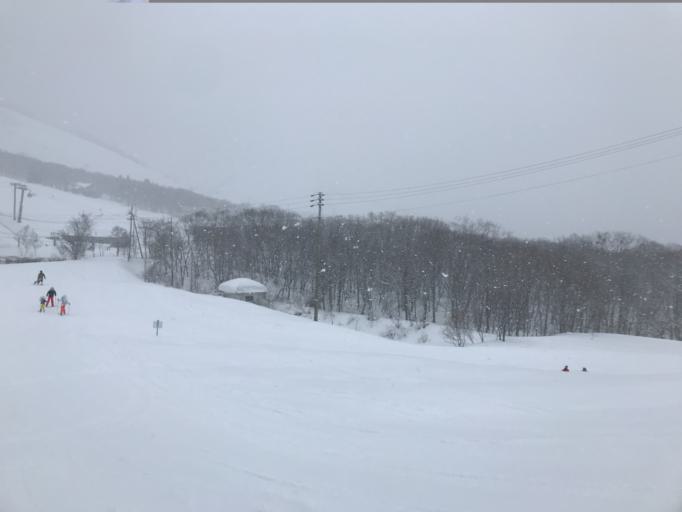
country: JP
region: Nagano
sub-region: Kitaazumi Gun
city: Hakuba
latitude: 36.7520
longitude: 137.8602
